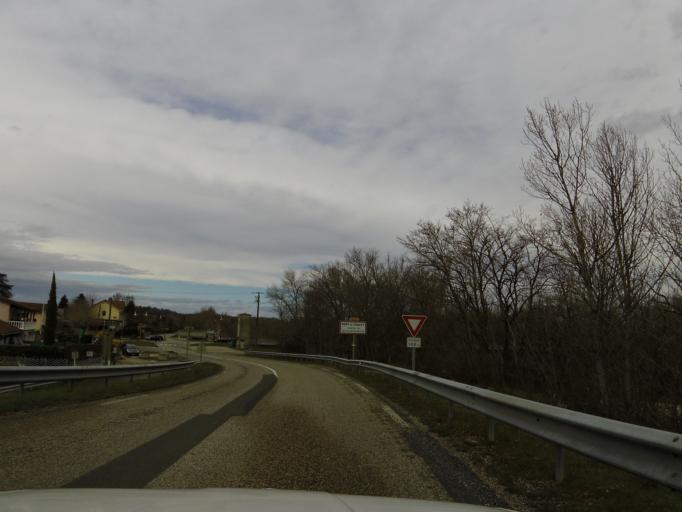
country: FR
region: Rhone-Alpes
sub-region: Departement de l'Ain
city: Chazey-sur-Ain
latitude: 45.9057
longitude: 5.2328
